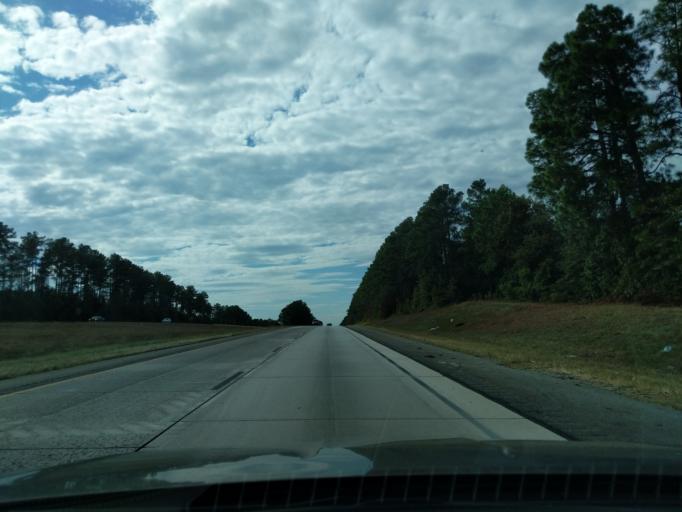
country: US
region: Georgia
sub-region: Columbia County
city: Grovetown
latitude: 33.4802
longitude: -82.1619
